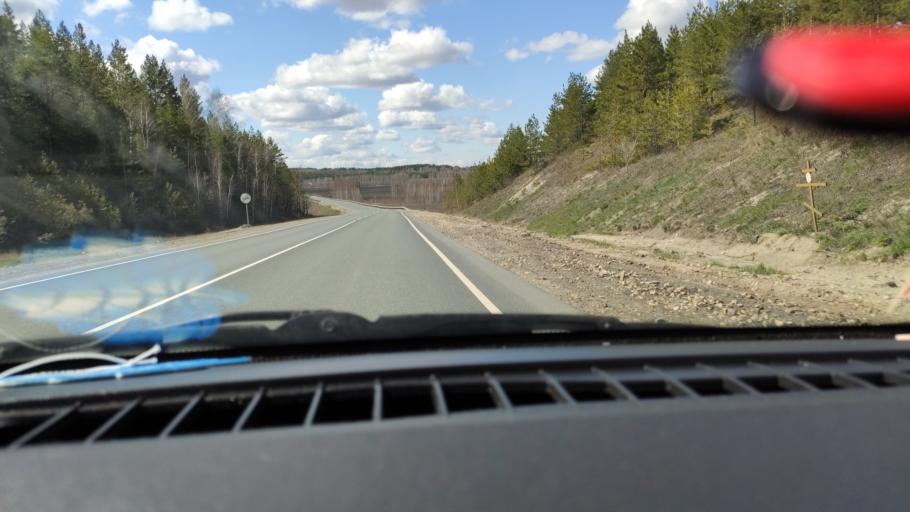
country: RU
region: Saratov
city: Khvalynsk
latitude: 52.5284
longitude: 48.0266
